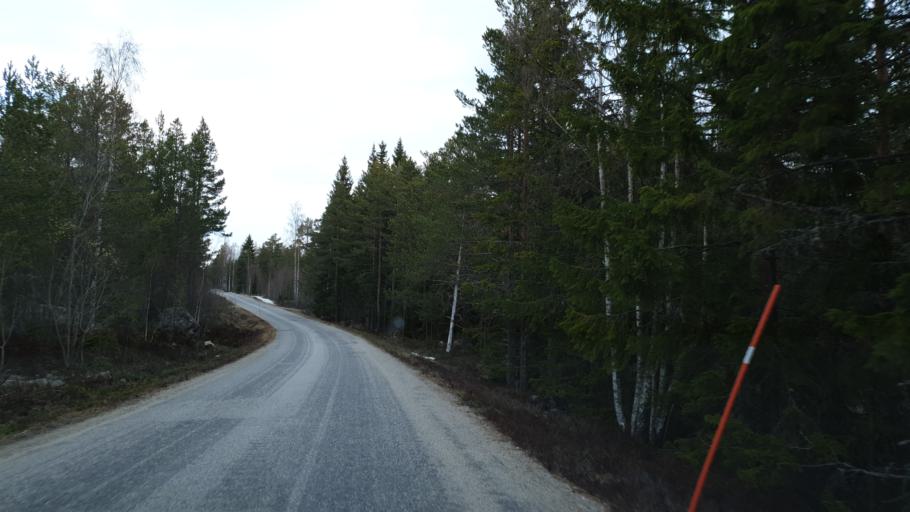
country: SE
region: Vaesternorrland
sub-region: Sundsvalls Kommun
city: Njurundabommen
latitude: 61.9693
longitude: 17.3817
